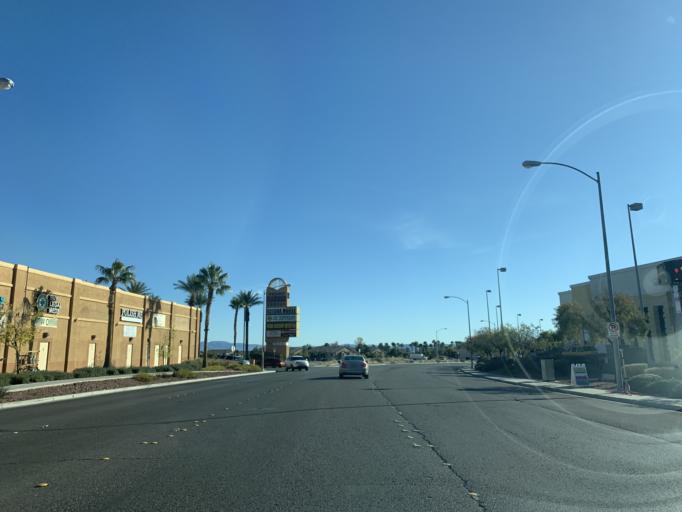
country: US
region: Nevada
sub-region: Clark County
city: Summerlin South
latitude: 36.1133
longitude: -115.3066
